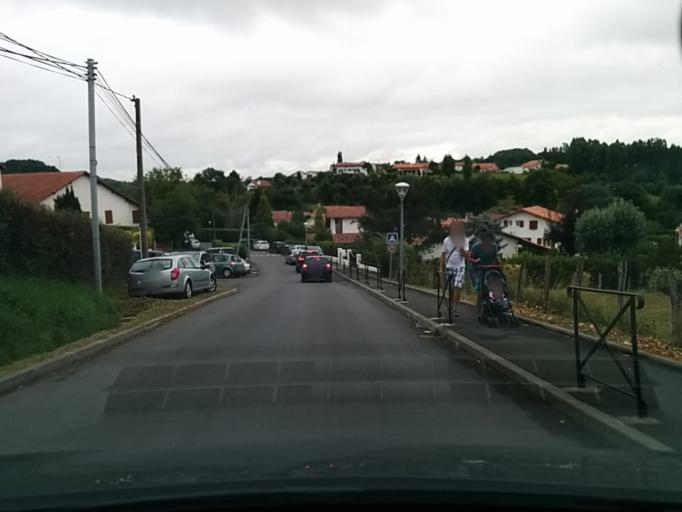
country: FR
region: Aquitaine
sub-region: Departement des Pyrenees-Atlantiques
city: Espelette
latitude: 43.3428
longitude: -1.4498
